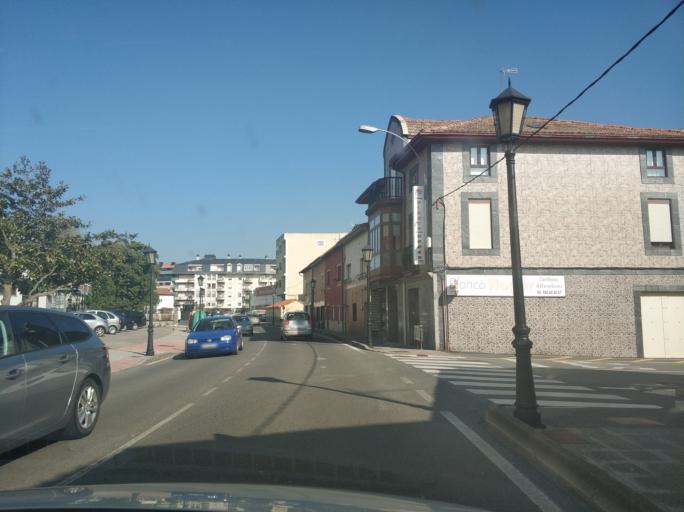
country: ES
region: Cantabria
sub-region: Provincia de Cantabria
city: Colindres
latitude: 43.3945
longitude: -3.4556
